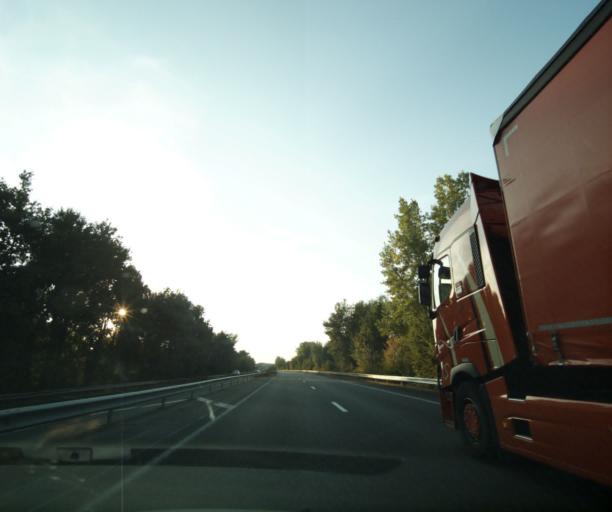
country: FR
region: Aquitaine
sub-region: Departement du Lot-et-Garonne
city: Layrac
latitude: 44.1223
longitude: 0.7124
